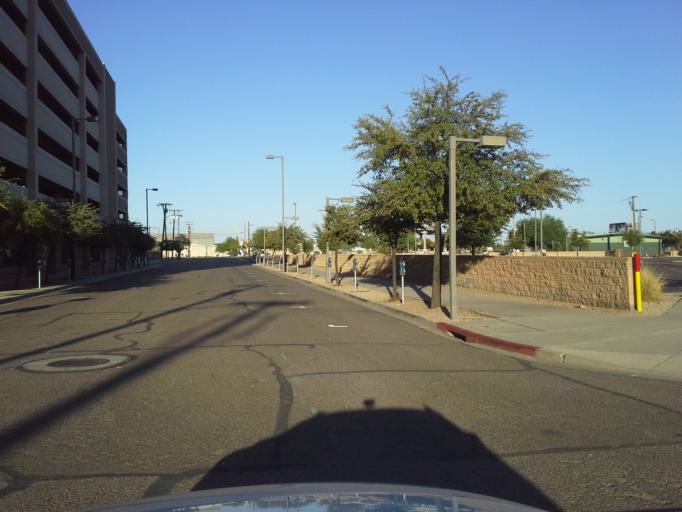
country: US
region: Arizona
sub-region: Maricopa County
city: Phoenix
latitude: 33.4432
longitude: -112.0687
